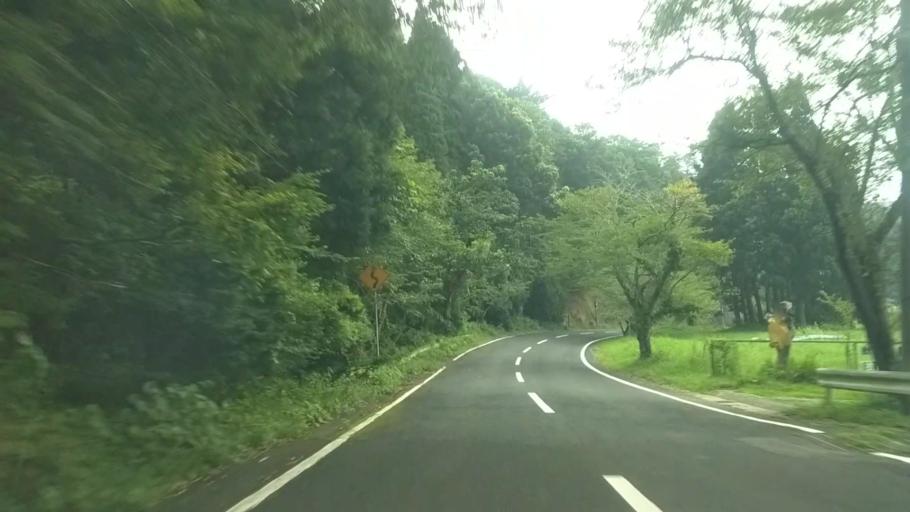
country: JP
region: Chiba
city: Kawaguchi
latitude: 35.1719
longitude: 140.1348
